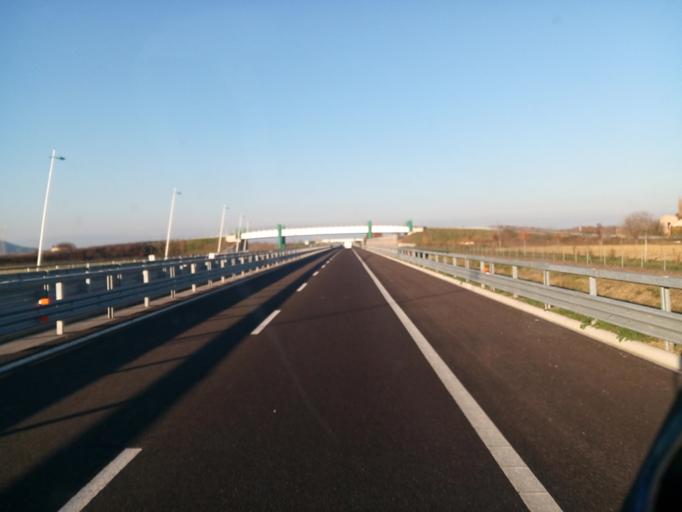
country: IT
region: Veneto
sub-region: Provincia di Vicenza
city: Villaganzerla
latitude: 45.4113
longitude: 11.6332
